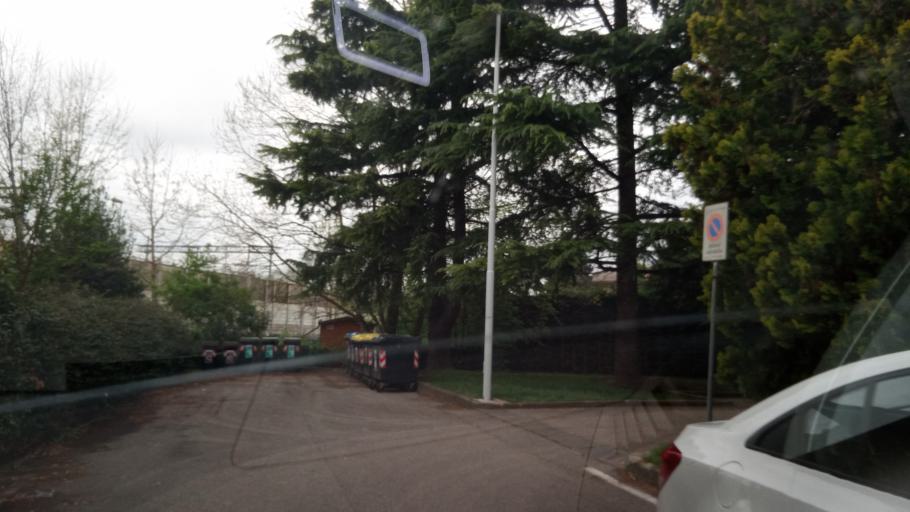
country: IT
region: Veneto
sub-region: Provincia di Padova
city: Cadoneghe
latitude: 45.4231
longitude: 11.9136
